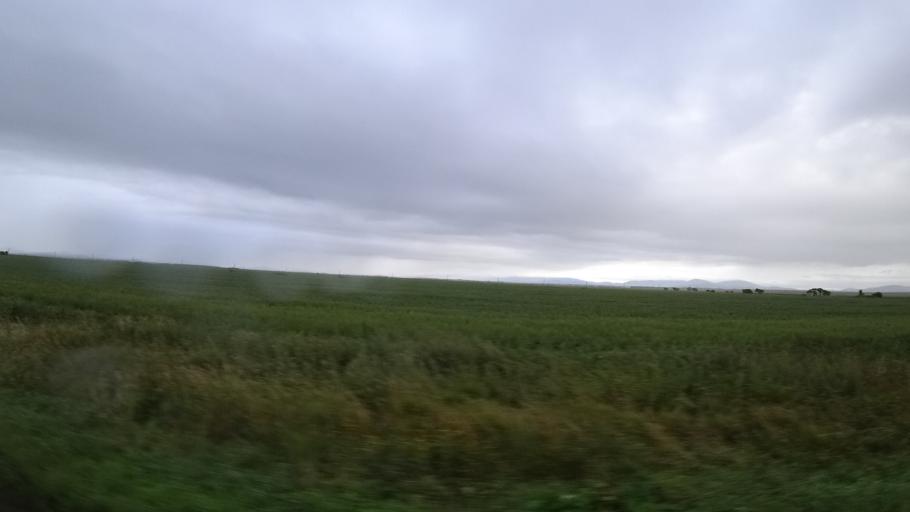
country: RU
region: Primorskiy
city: Chernigovka
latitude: 44.3842
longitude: 132.5295
